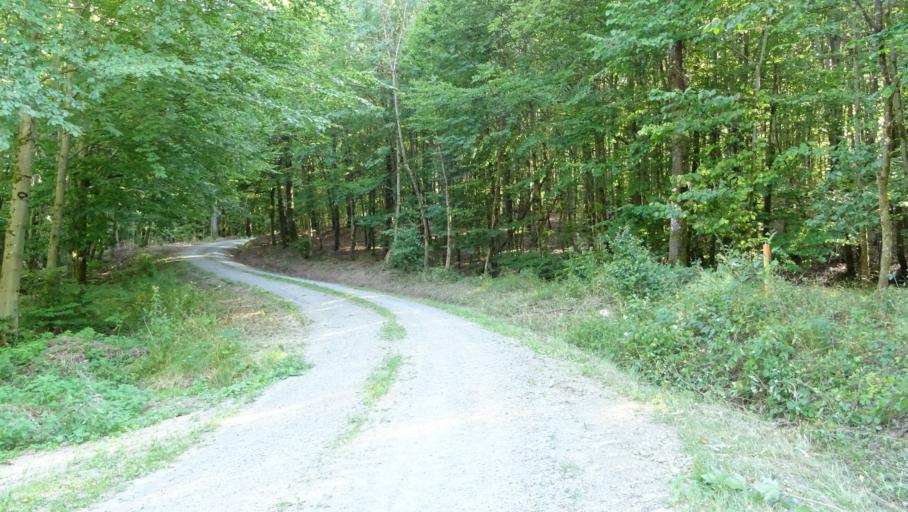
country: DE
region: Baden-Wuerttemberg
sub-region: Karlsruhe Region
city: Fahrenbach
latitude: 49.4130
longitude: 9.1223
